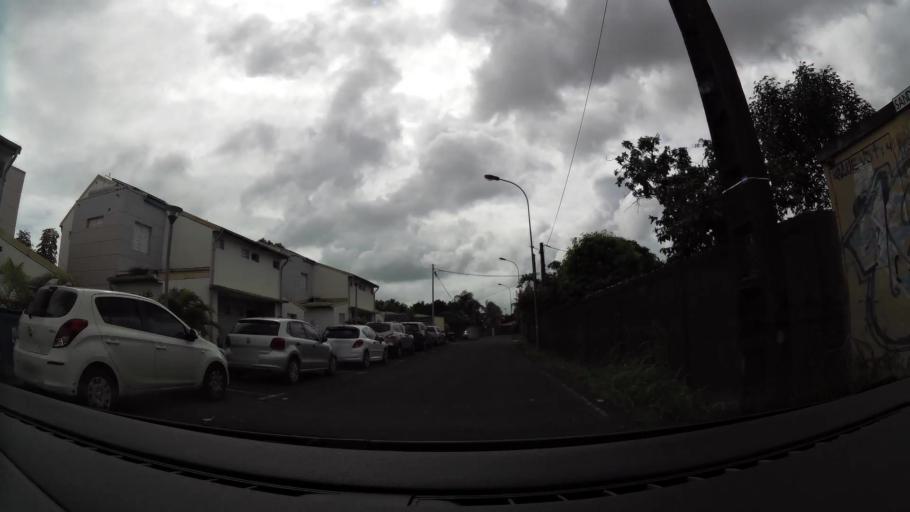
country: GP
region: Guadeloupe
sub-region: Guadeloupe
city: Baie-Mahault
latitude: 16.2598
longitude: -61.5742
